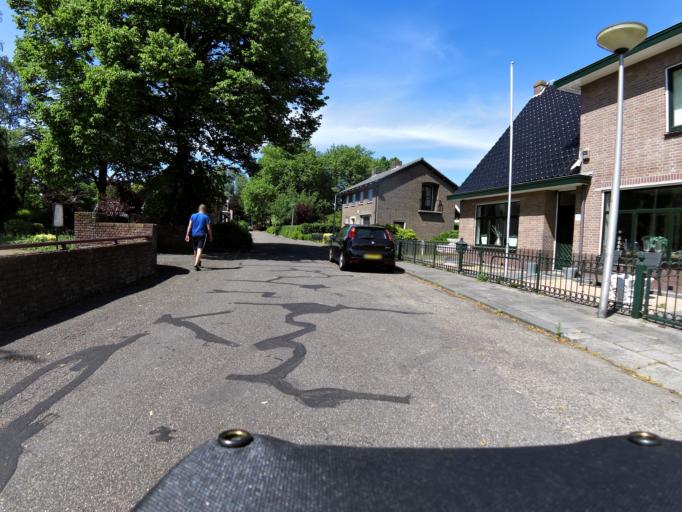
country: NL
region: South Holland
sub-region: Gemeente Maassluis
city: Maassluis
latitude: 51.9022
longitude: 4.2540
